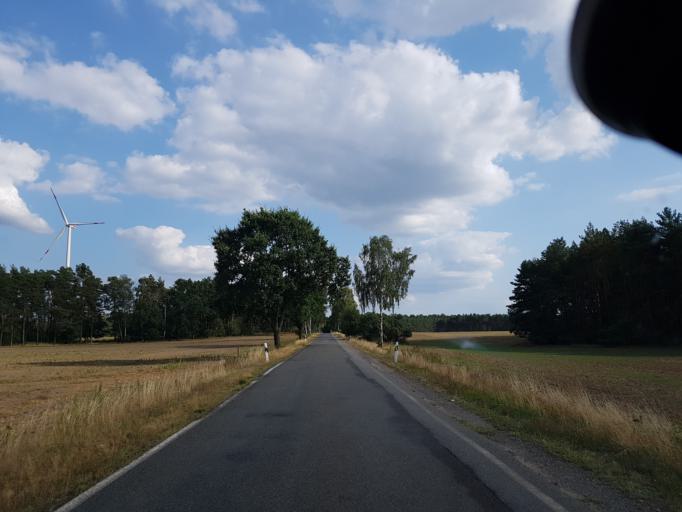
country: DE
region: Brandenburg
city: Bronkow
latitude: 51.6929
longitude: 13.8830
